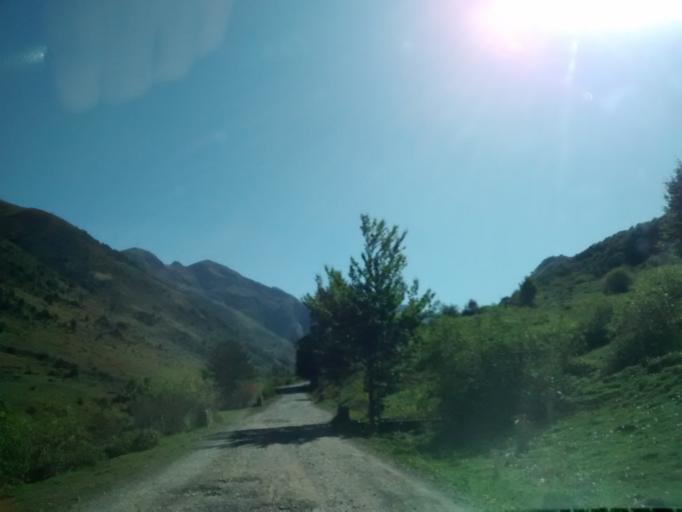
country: ES
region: Aragon
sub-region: Provincia de Huesca
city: Aragues del Puerto
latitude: 42.8520
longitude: -0.6784
